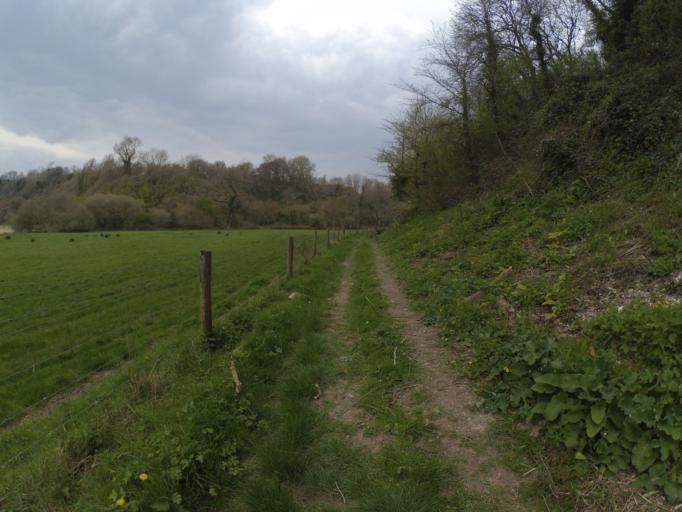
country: GB
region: England
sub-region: West Sussex
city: Arundel
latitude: 50.8821
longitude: -0.5270
